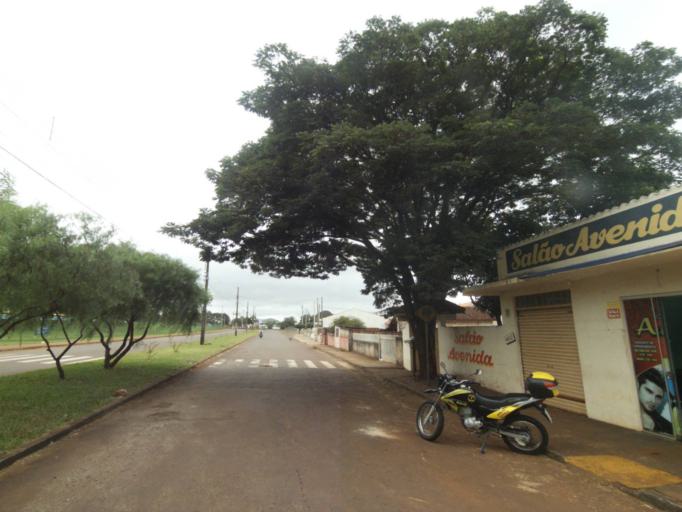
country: BR
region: Parana
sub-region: Campo Mourao
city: Campo Mourao
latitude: -24.0224
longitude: -52.3559
